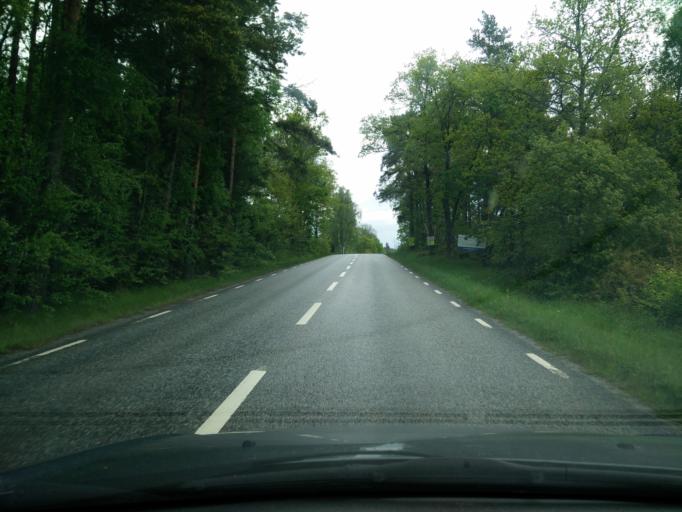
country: SE
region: Stockholm
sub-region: Norrtalje Kommun
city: Norrtalje
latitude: 59.7801
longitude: 18.7698
